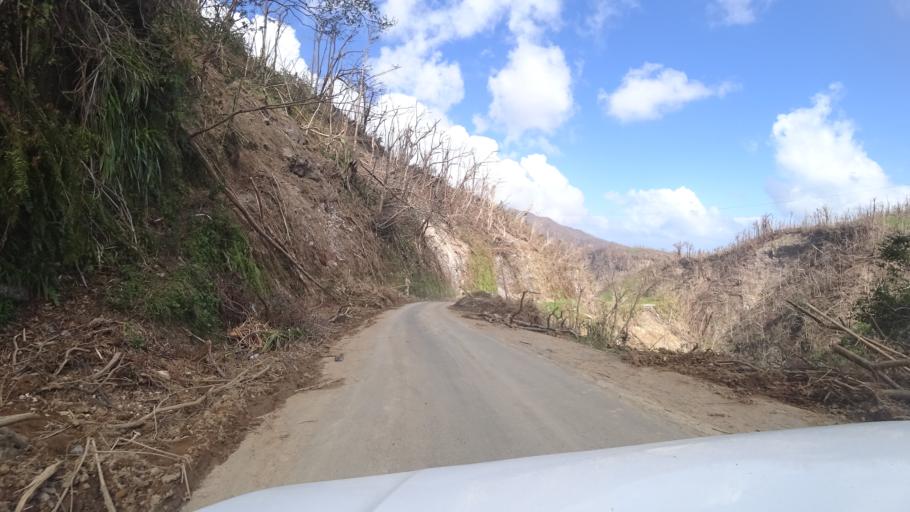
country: DM
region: Saint Patrick
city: Berekua
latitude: 15.2653
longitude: -61.3364
